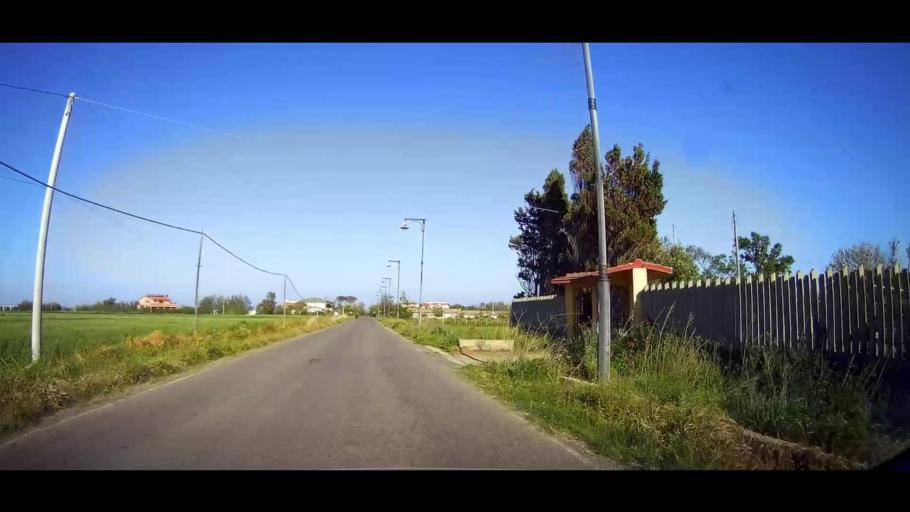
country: IT
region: Calabria
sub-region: Provincia di Crotone
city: Crotone
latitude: 39.0254
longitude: 17.1904
